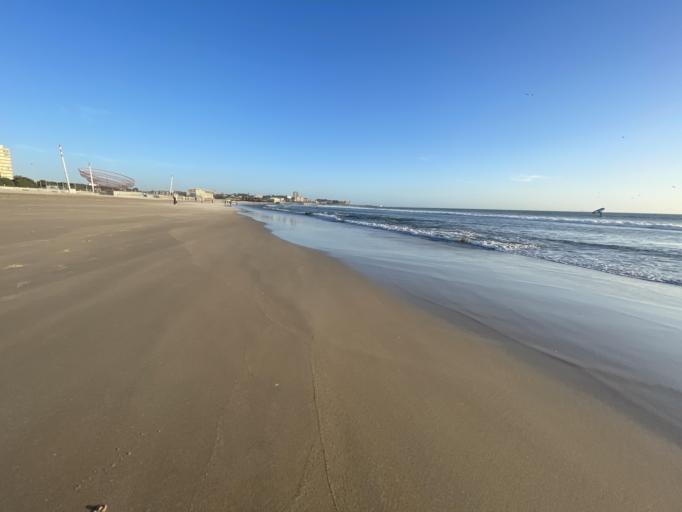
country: PT
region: Porto
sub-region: Matosinhos
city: Matosinhos
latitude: 41.1753
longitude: -8.6926
